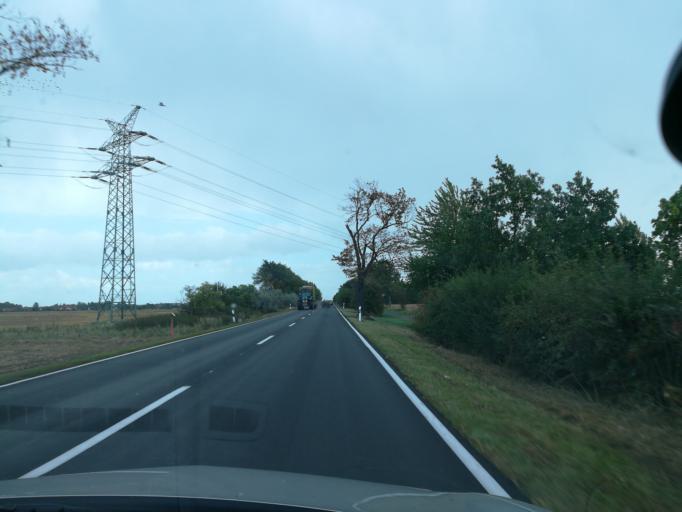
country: DE
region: Saxony-Anhalt
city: Ebendorf
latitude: 52.1945
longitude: 11.5623
